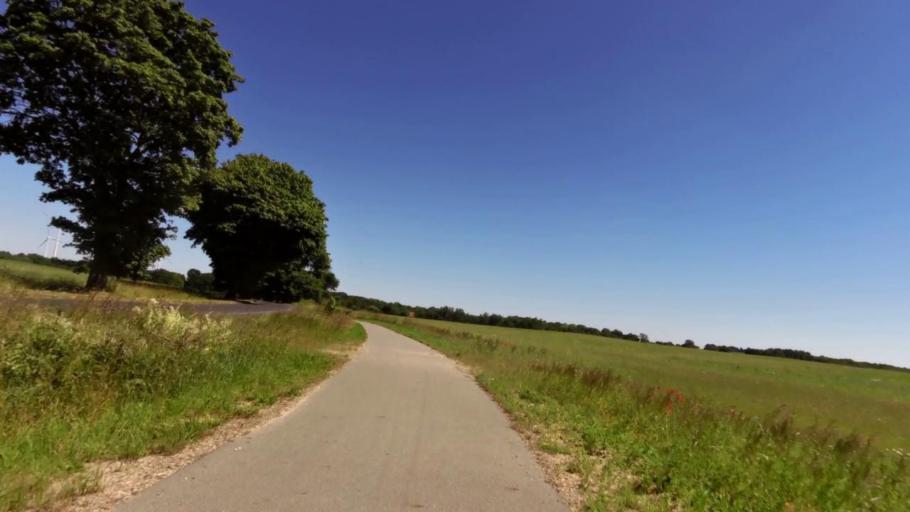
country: PL
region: West Pomeranian Voivodeship
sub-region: Powiat kolobrzeski
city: Goscino
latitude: 54.0343
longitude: 15.6777
